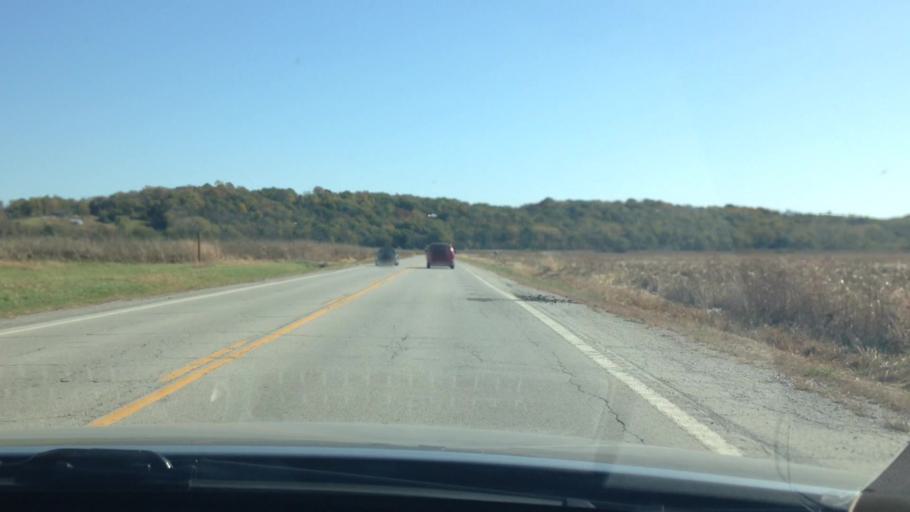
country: US
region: Kansas
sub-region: Leavenworth County
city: Leavenworth
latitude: 39.3185
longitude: -94.8579
